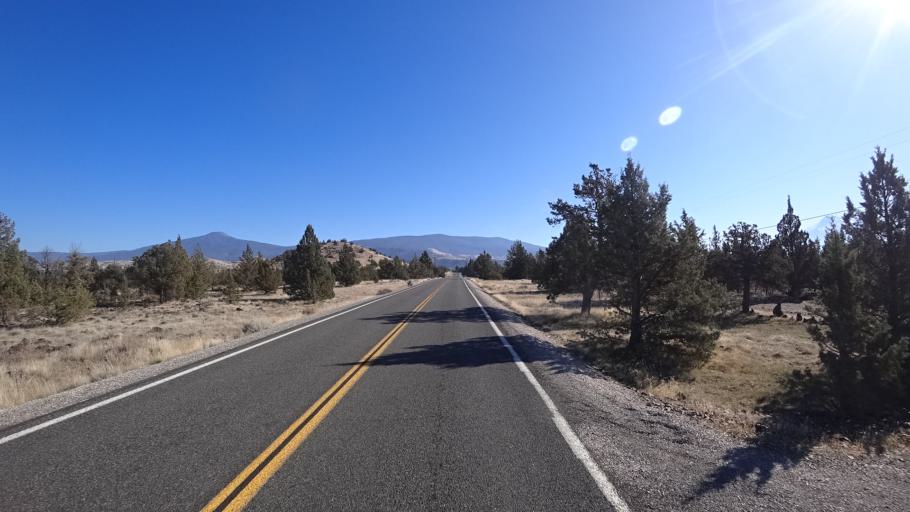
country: US
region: California
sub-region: Siskiyou County
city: Montague
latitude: 41.6598
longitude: -122.3800
